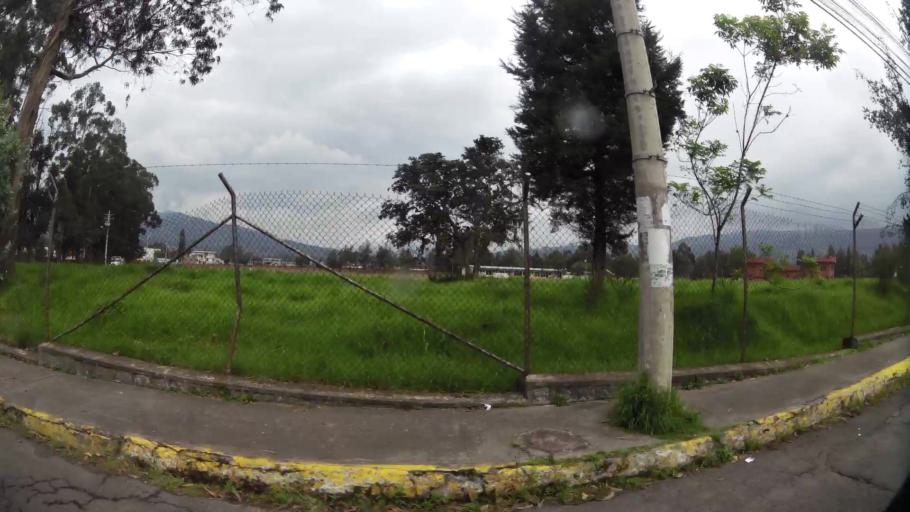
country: EC
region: Pichincha
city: Sangolqui
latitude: -0.3518
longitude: -78.4749
